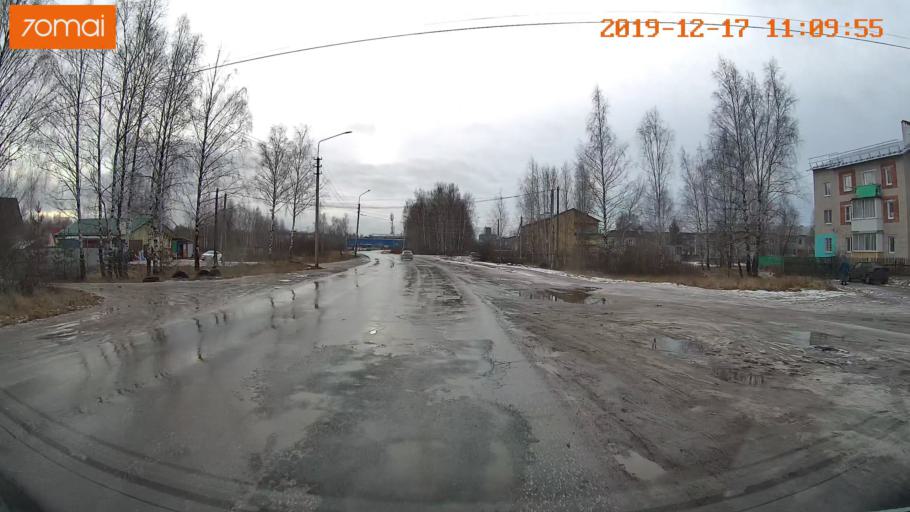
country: RU
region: Vladimir
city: Gus'-Khrustal'nyy
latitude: 55.5967
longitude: 40.6413
